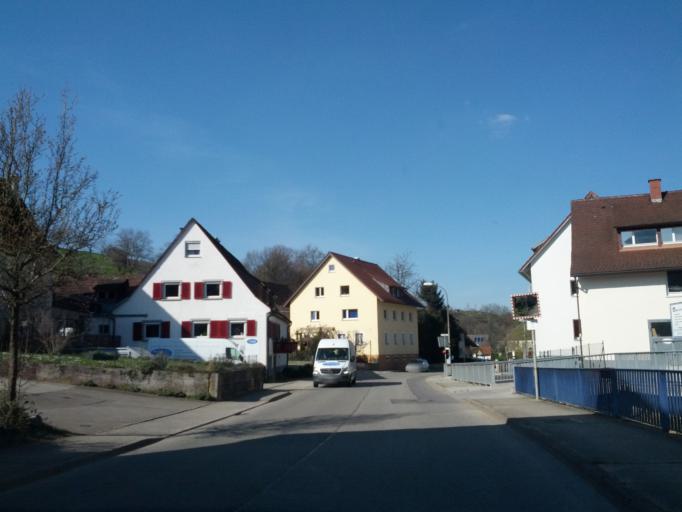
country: DE
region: Baden-Wuerttemberg
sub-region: Freiburg Region
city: Au
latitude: 47.9543
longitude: 7.8286
